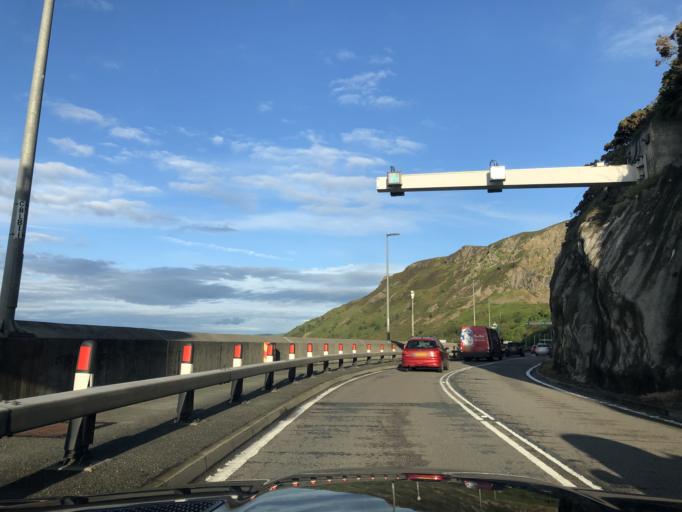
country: GB
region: Wales
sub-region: Conwy
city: Conwy
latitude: 53.2890
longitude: -3.8787
